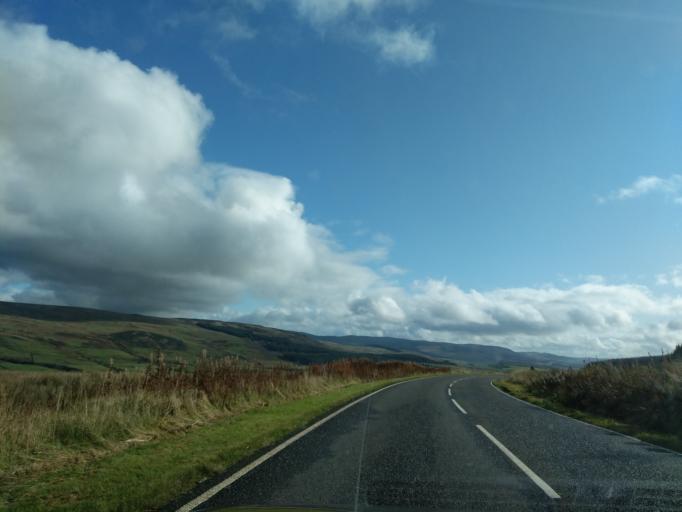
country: GB
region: Scotland
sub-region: Dumfries and Galloway
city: Moffat
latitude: 55.3849
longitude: -3.4858
